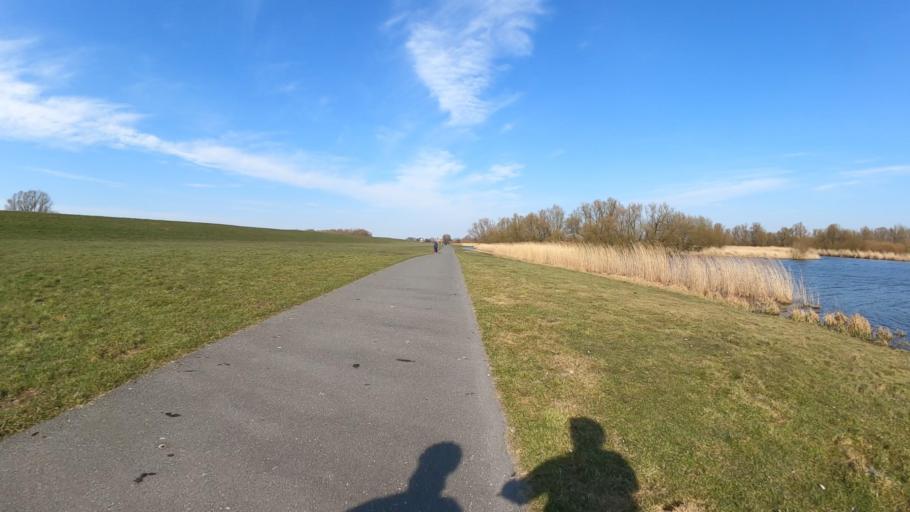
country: DE
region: Schleswig-Holstein
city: Haseldorf
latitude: 53.6304
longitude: 9.5778
